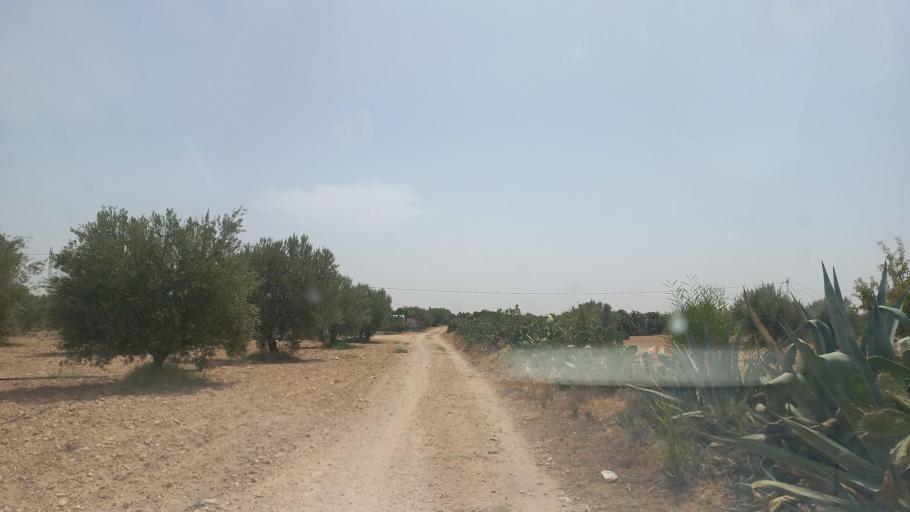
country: TN
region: Al Qasrayn
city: Kasserine
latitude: 35.2589
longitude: 9.0064
